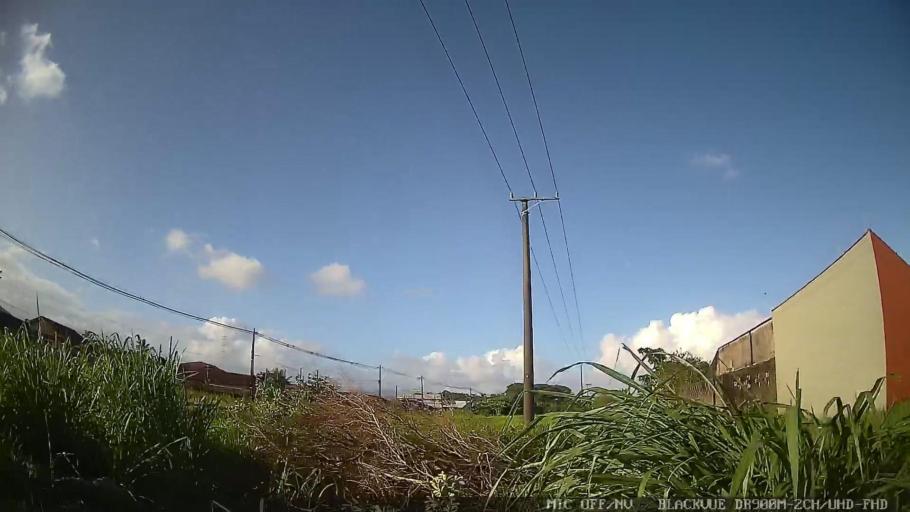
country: BR
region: Sao Paulo
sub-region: Itanhaem
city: Itanhaem
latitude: -24.1502
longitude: -46.7278
